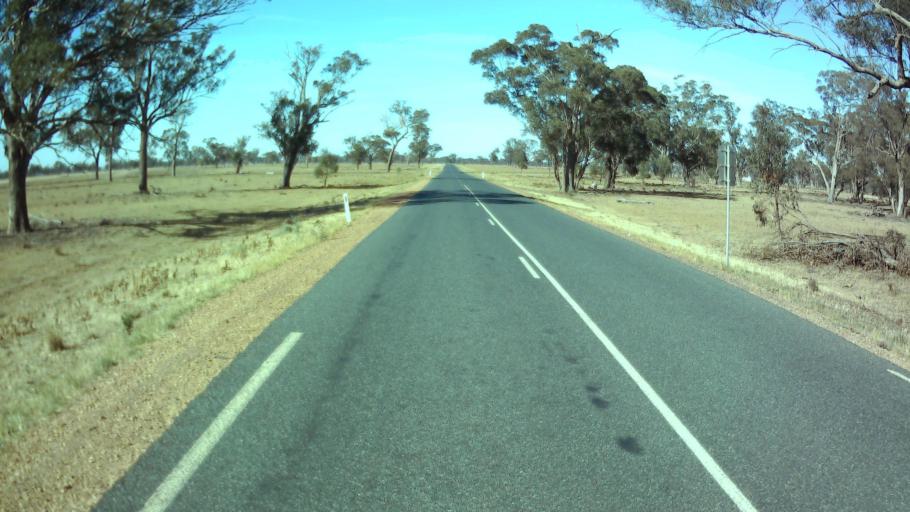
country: AU
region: New South Wales
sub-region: Weddin
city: Grenfell
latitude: -34.0431
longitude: 147.9279
